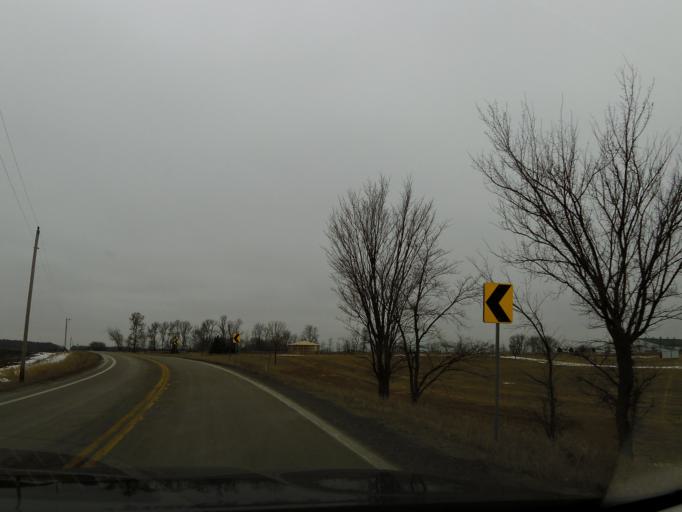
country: US
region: Minnesota
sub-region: Carver County
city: Watertown
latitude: 45.0127
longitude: -93.8484
